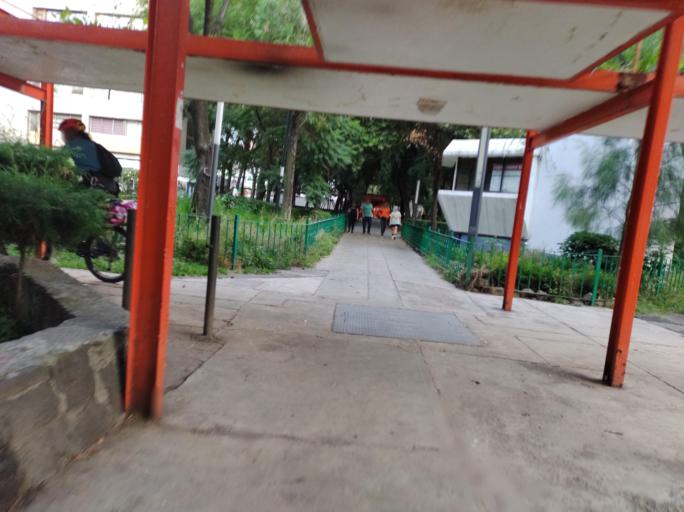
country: MX
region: Mexico City
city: Cuauhtemoc
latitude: 19.4540
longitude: -99.1444
